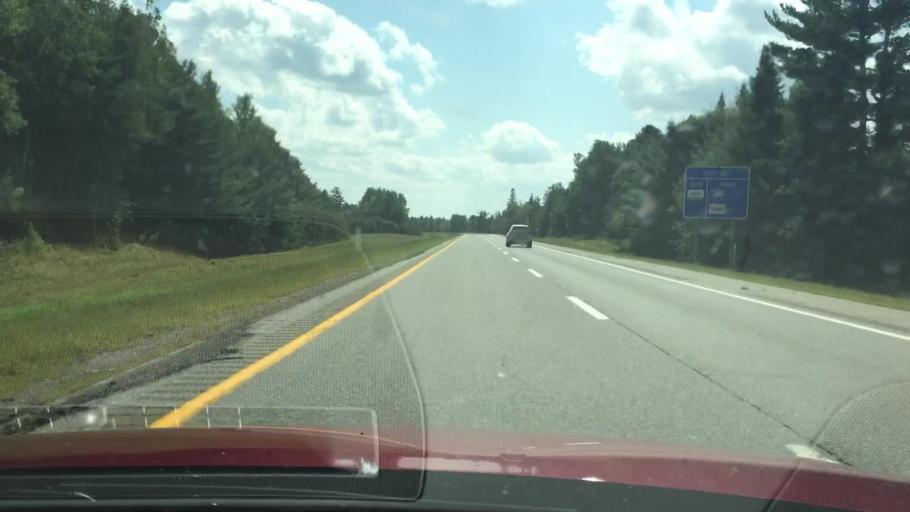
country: US
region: Maine
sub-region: Penobscot County
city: Lincoln
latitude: 45.3897
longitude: -68.6037
